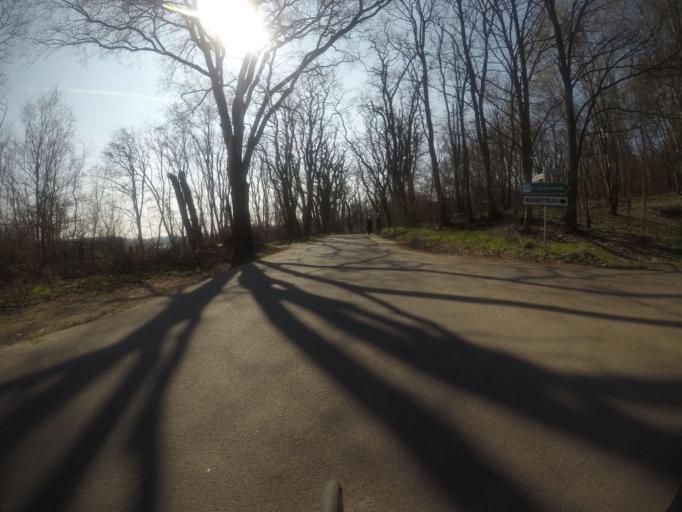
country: DE
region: Berlin
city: Muggelheim
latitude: 52.3862
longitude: 13.7016
